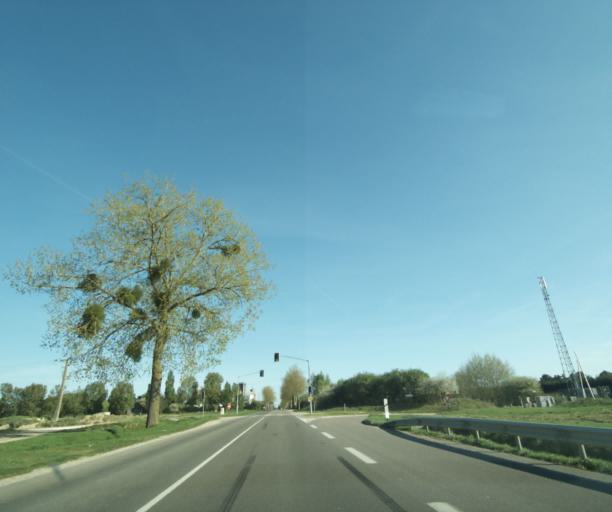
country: FR
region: Ile-de-France
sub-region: Departement de Seine-et-Marne
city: Nangis
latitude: 48.5677
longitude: 3.0050
